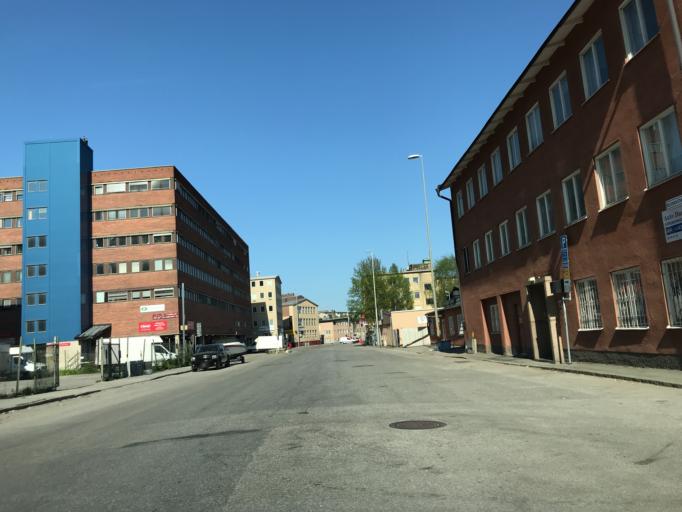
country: SE
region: Stockholm
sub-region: Stockholms Kommun
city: Arsta
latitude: 59.2984
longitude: 18.0148
